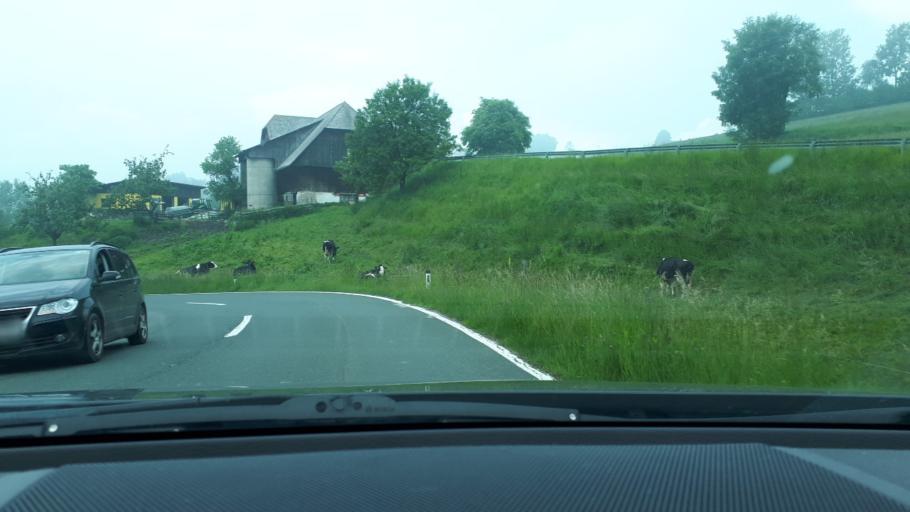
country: AT
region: Carinthia
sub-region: Politischer Bezirk Wolfsberg
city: Preitenegg
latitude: 46.9376
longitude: 14.9099
